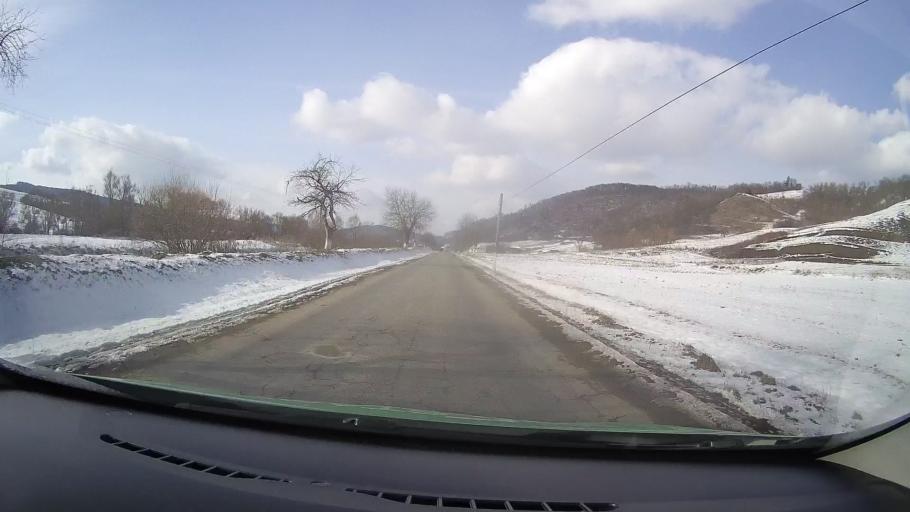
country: RO
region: Sibiu
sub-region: Comuna Iacobeni
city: Iacobeni
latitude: 46.0413
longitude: 24.7303
